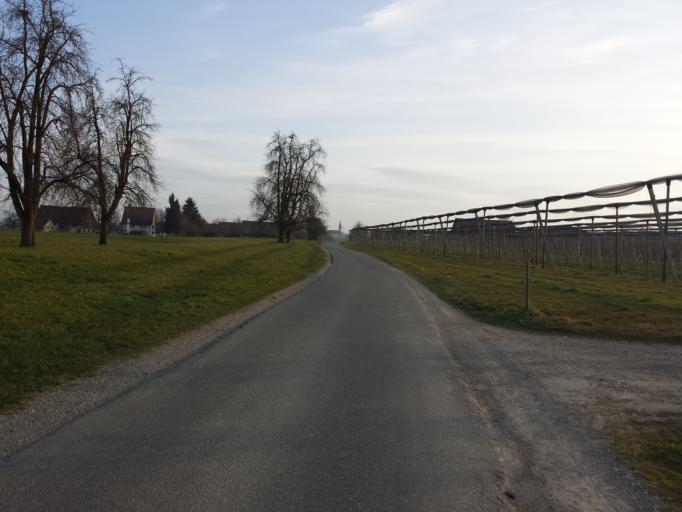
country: CH
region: Thurgau
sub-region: Arbon District
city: Salmsach
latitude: 47.5458
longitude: 9.3569
